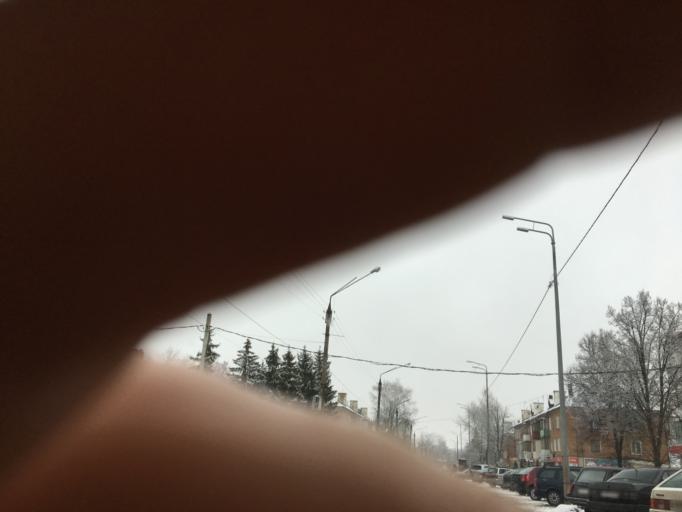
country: RU
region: Tula
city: Donskoy
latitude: 53.9676
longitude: 38.3195
